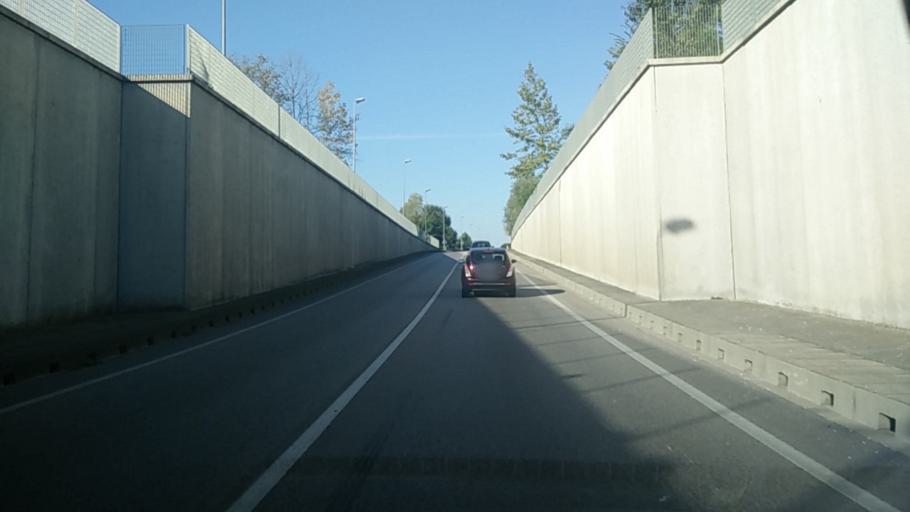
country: IT
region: Veneto
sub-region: Provincia di Padova
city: Piombino Dese
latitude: 45.6187
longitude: 11.9832
